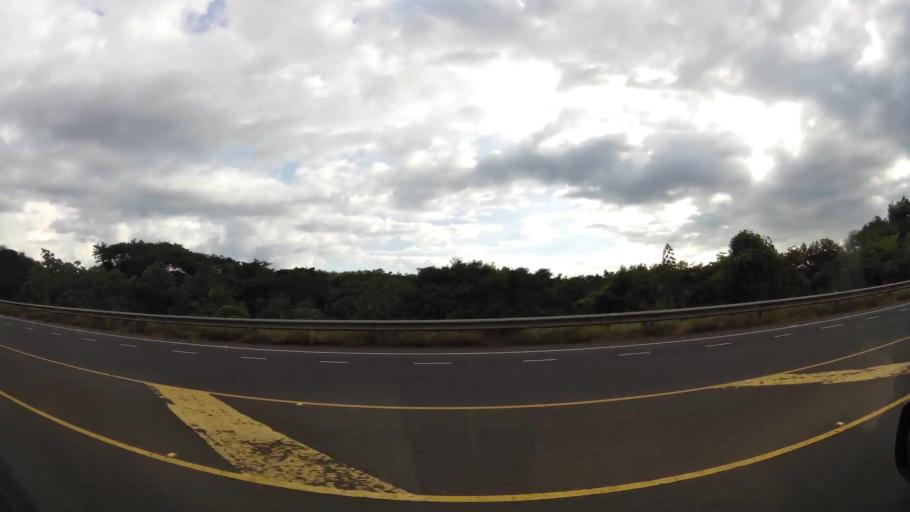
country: CR
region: Alajuela
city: Orotina
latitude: 9.8858
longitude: -84.5879
